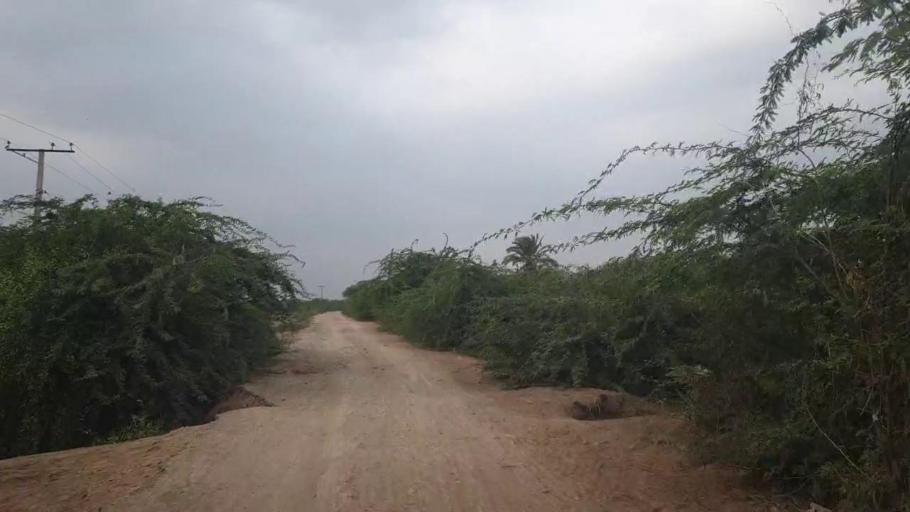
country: PK
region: Sindh
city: Badin
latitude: 24.6145
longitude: 68.6844
